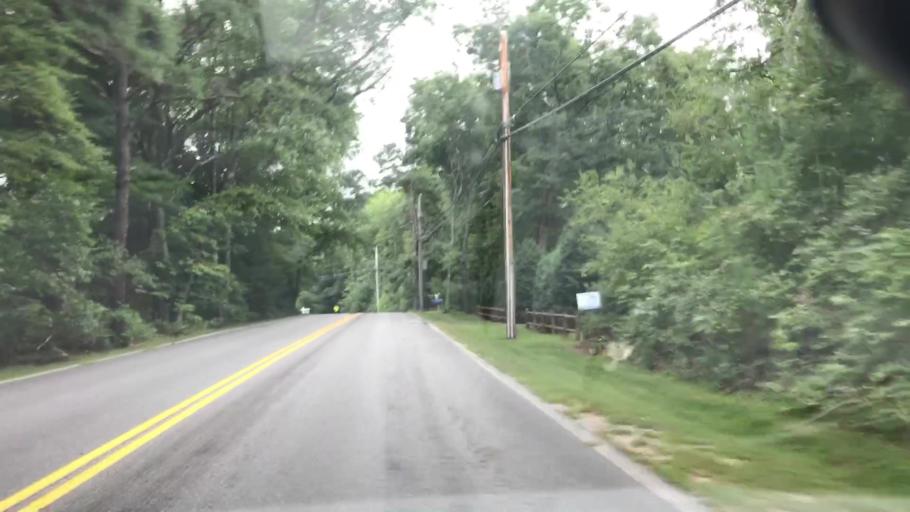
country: US
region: New Hampshire
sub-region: Hillsborough County
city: Hollis
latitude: 42.8158
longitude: -71.5601
